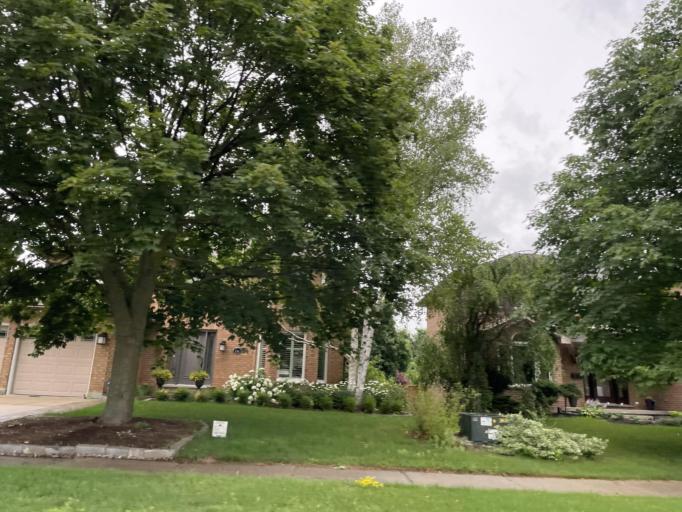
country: CA
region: Ontario
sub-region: Wellington County
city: Guelph
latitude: 43.4997
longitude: -80.2370
